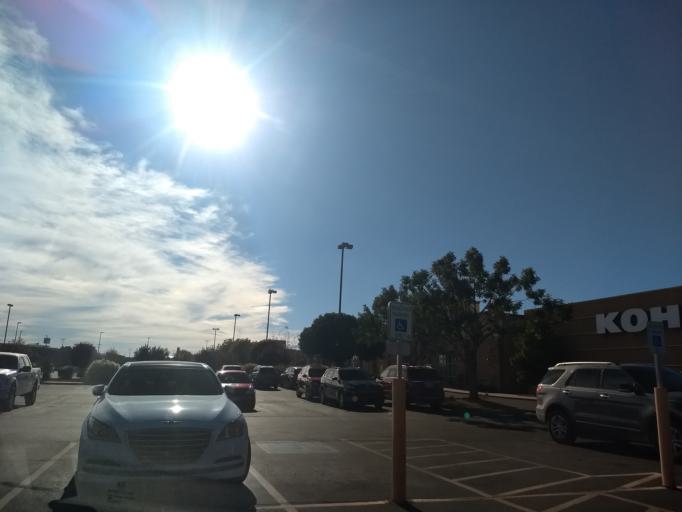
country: US
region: Utah
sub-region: Washington County
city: Washington
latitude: 37.1296
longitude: -113.5210
